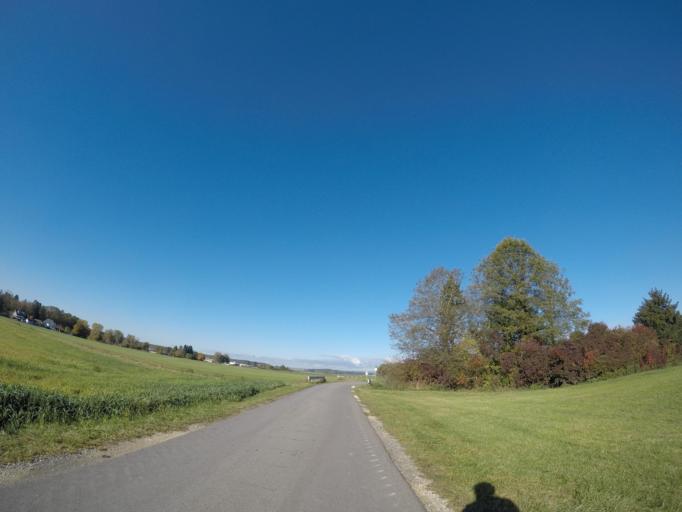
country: DE
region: Baden-Wuerttemberg
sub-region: Tuebingen Region
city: Saulgau
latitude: 48.0275
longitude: 9.5140
